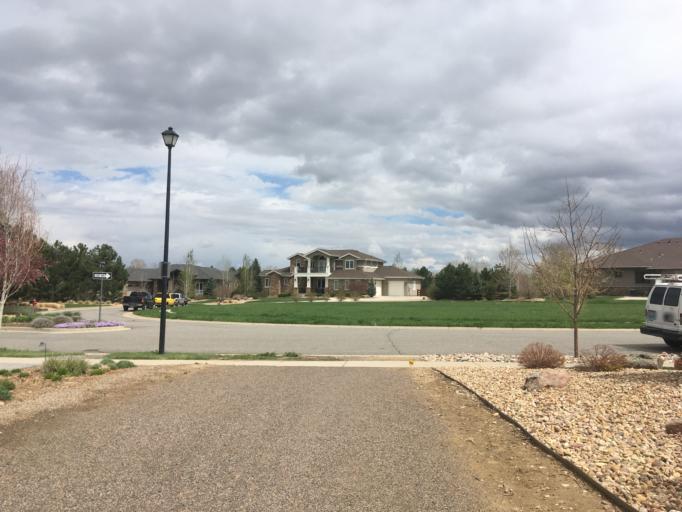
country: US
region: Colorado
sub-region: Boulder County
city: Lafayette
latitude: 40.0209
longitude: -105.1212
